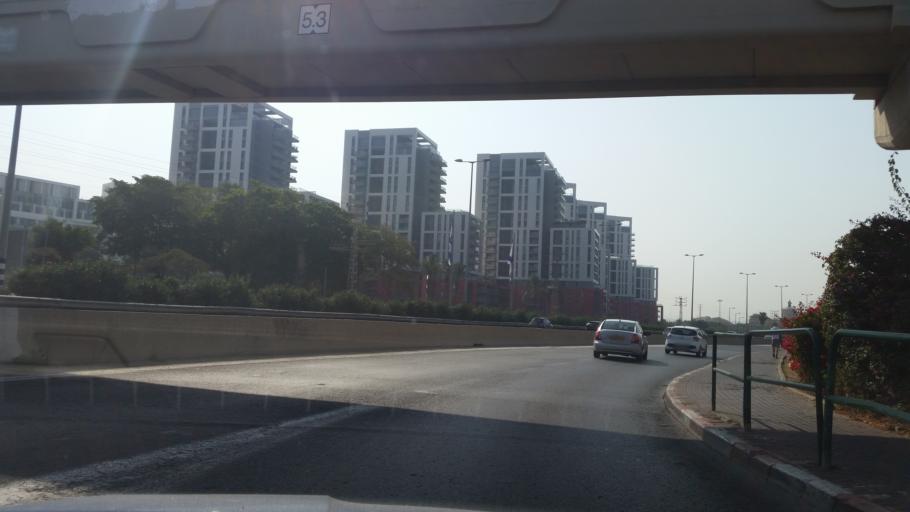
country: IL
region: Tel Aviv
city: Herzliyya
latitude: 32.1650
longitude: 34.8134
